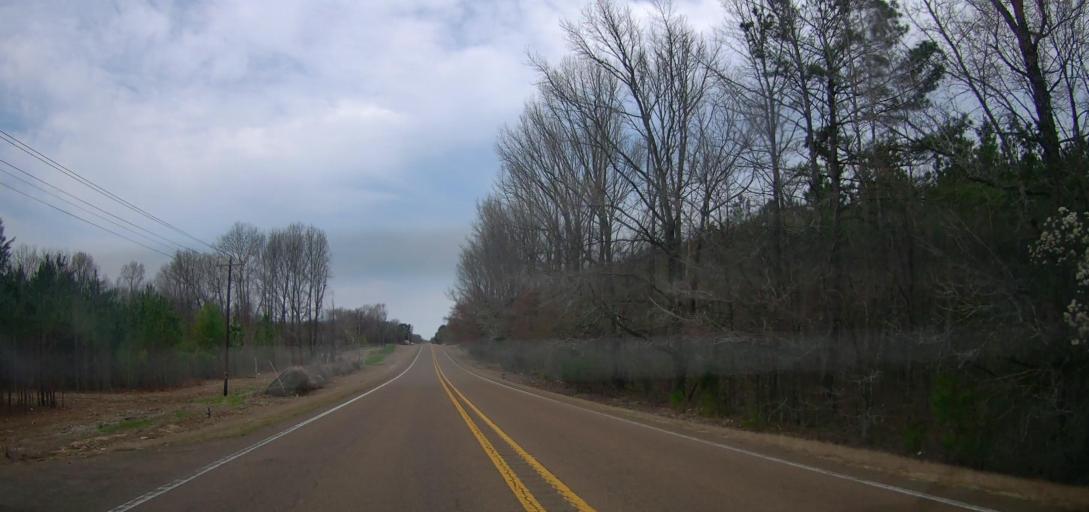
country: US
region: Mississippi
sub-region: Marshall County
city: Byhalia
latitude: 34.8512
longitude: -89.6331
